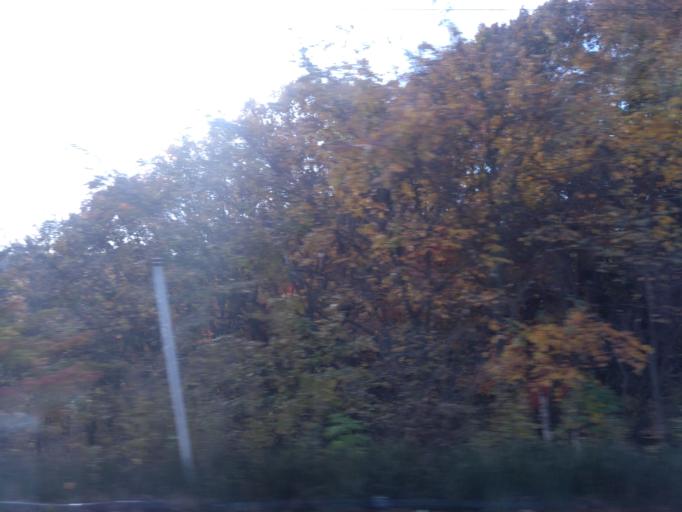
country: JP
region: Hokkaido
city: Kitahiroshima
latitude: 42.9884
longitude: 141.5593
